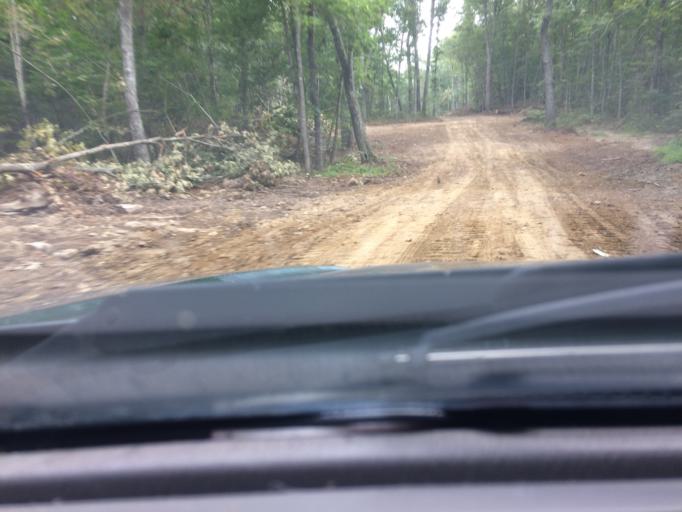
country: US
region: Tennessee
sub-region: Fentress County
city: Grimsley
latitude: 36.1863
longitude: -84.8973
